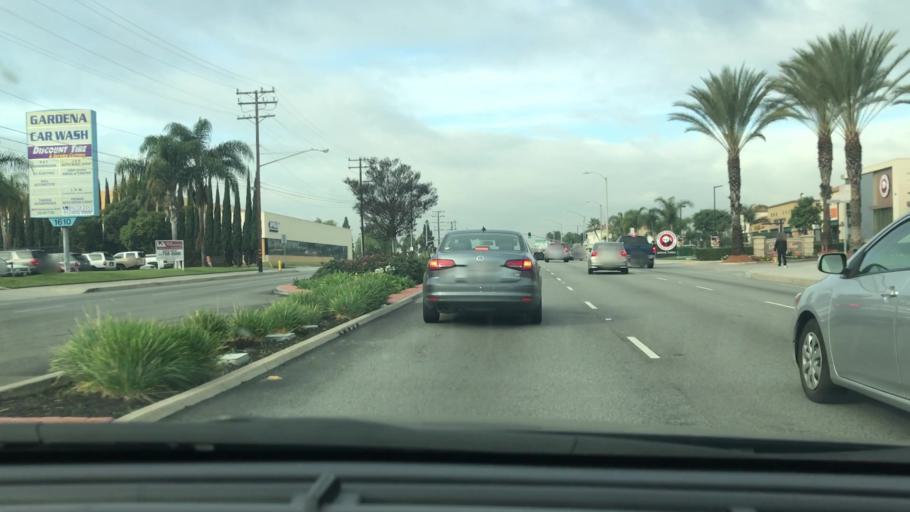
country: US
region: California
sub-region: Los Angeles County
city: Gardena
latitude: 33.8729
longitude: -118.3051
